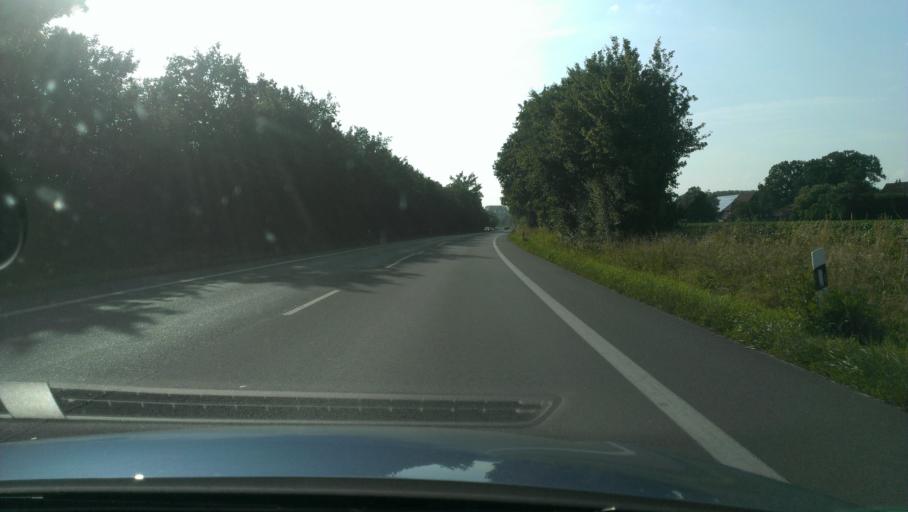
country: DE
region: North Rhine-Westphalia
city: Sendenhorst
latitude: 51.8273
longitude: 7.8829
